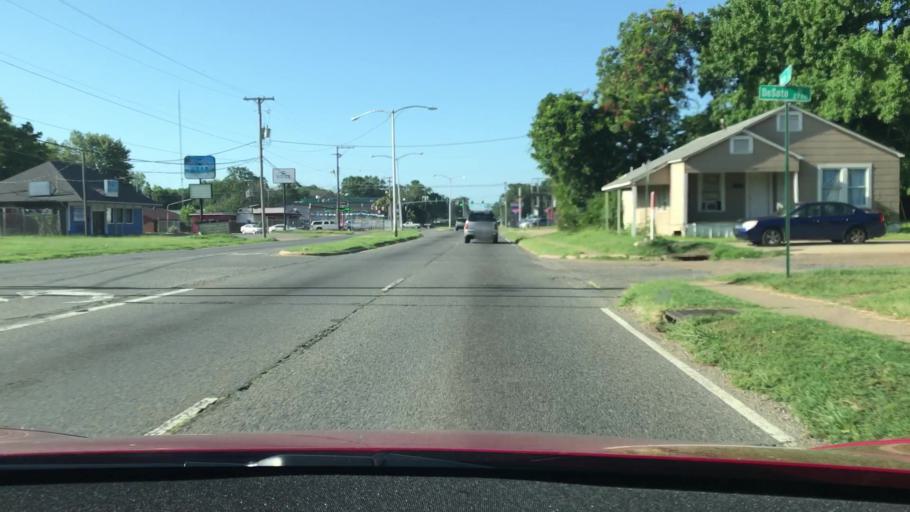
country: US
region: Louisiana
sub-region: Caddo Parish
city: Shreveport
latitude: 32.4729
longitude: -93.7801
